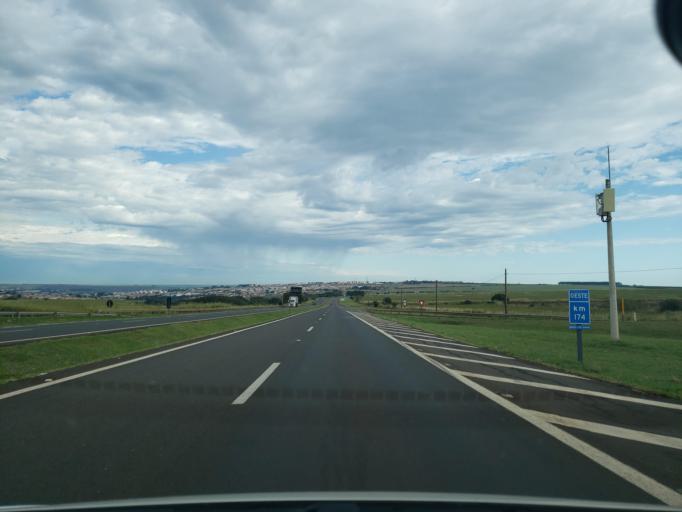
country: BR
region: Sao Paulo
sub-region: Jau
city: Jau
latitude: -22.2654
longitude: -48.5160
